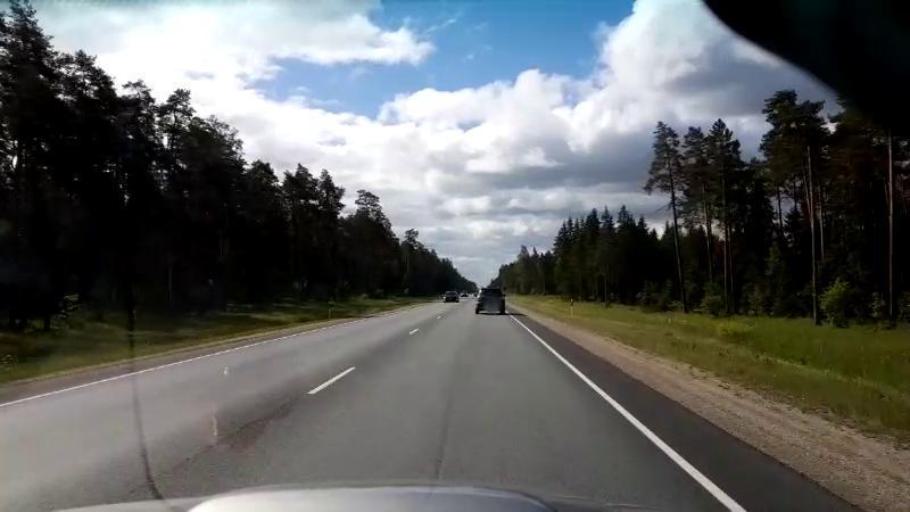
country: EE
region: Raplamaa
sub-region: Maerjamaa vald
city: Marjamaa
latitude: 59.0106
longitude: 24.4561
